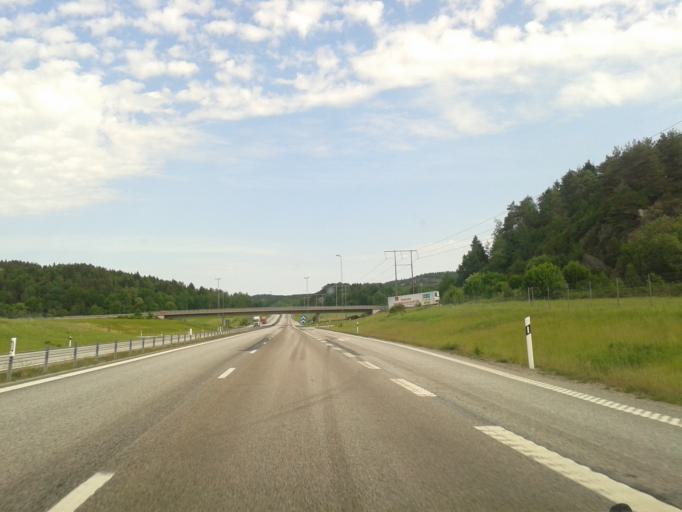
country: SE
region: Vaestra Goetaland
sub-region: Munkedals Kommun
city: Munkedal
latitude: 58.5188
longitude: 11.5500
